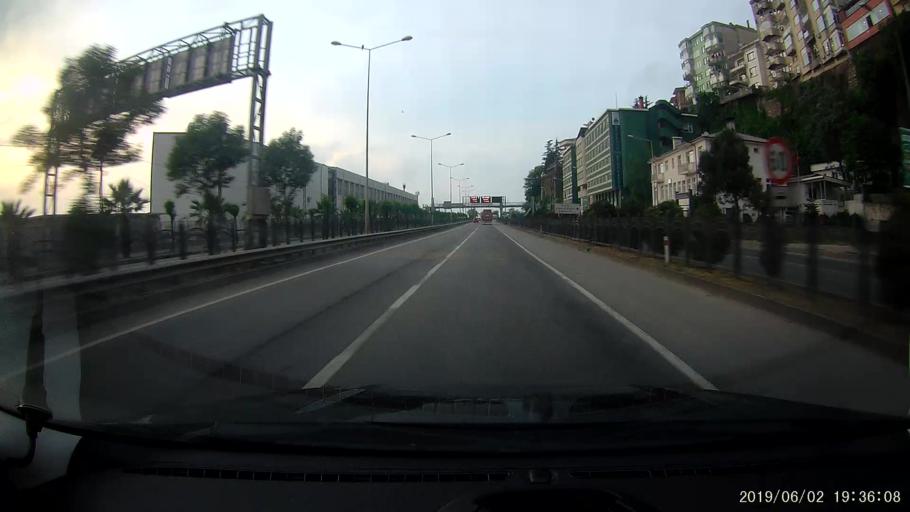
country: TR
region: Giresun
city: Giresun
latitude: 40.9202
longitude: 38.3855
